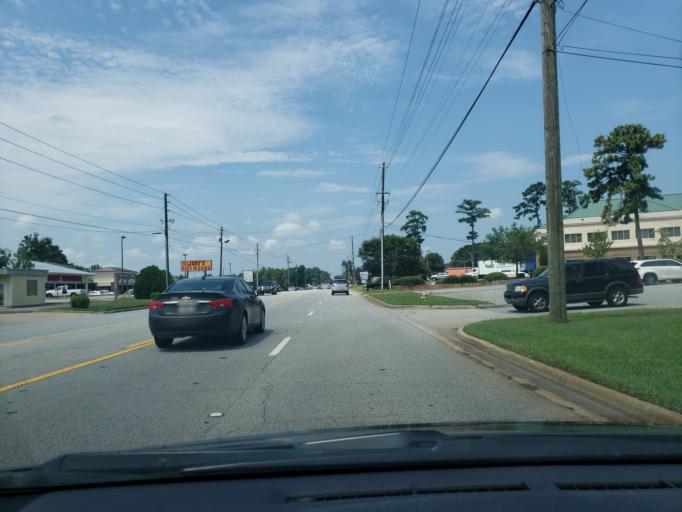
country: US
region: Georgia
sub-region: Dougherty County
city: Albany
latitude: 31.6136
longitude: -84.2189
